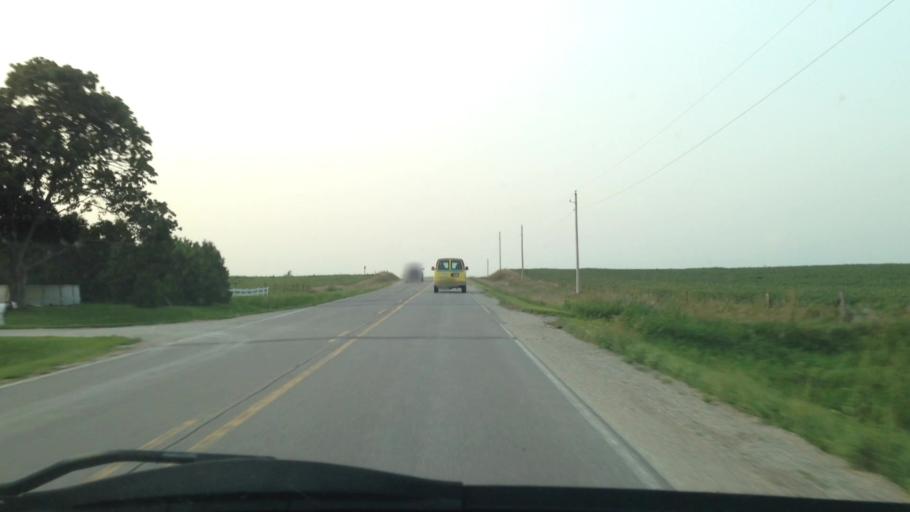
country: US
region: Iowa
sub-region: Benton County
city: Atkins
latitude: 42.0118
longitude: -91.8737
